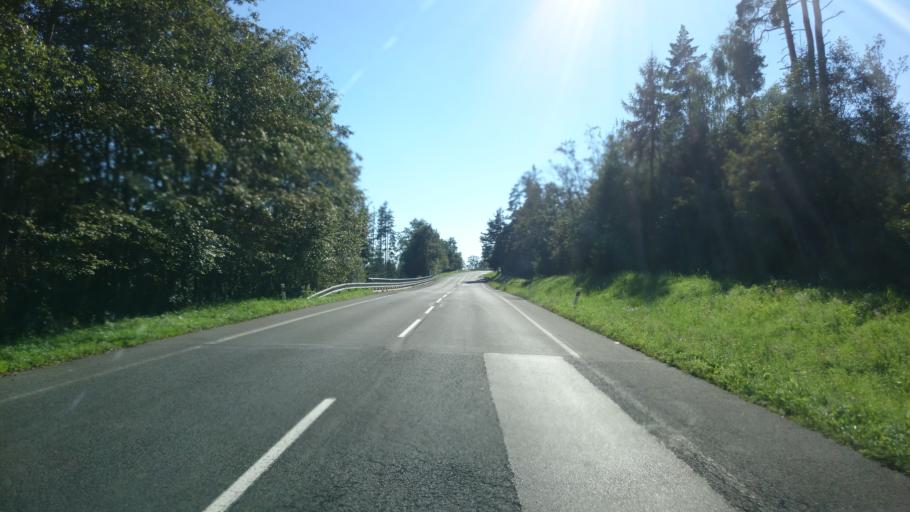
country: SK
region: Presovsky
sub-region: Okres Poprad
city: Vysoke Tatry
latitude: 49.1470
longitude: 20.2498
